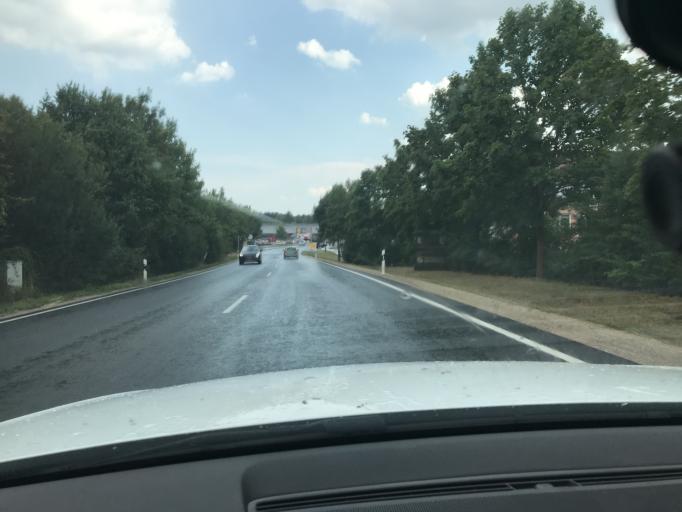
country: DE
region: Bavaria
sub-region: Upper Palatinate
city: Grafenwohr
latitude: 49.7308
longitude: 11.9018
